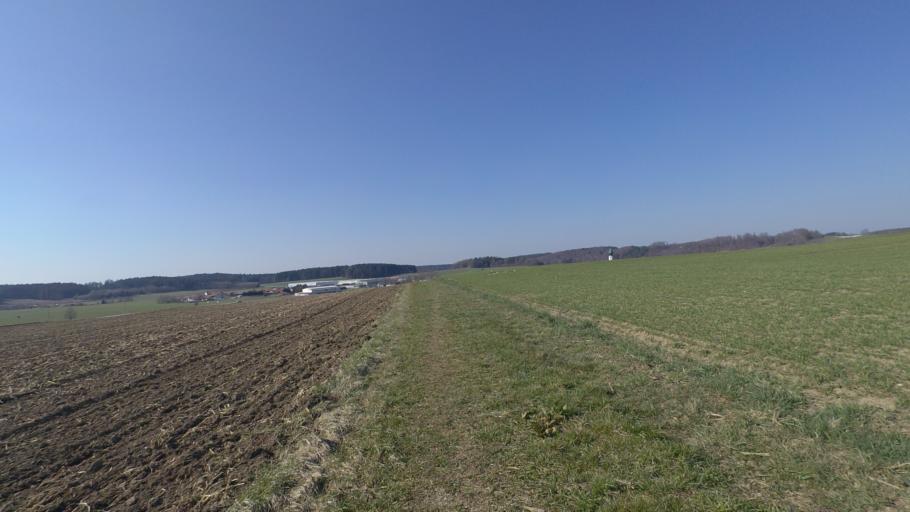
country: DE
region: Bavaria
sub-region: Upper Bavaria
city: Vachendorf
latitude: 47.8677
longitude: 12.5896
